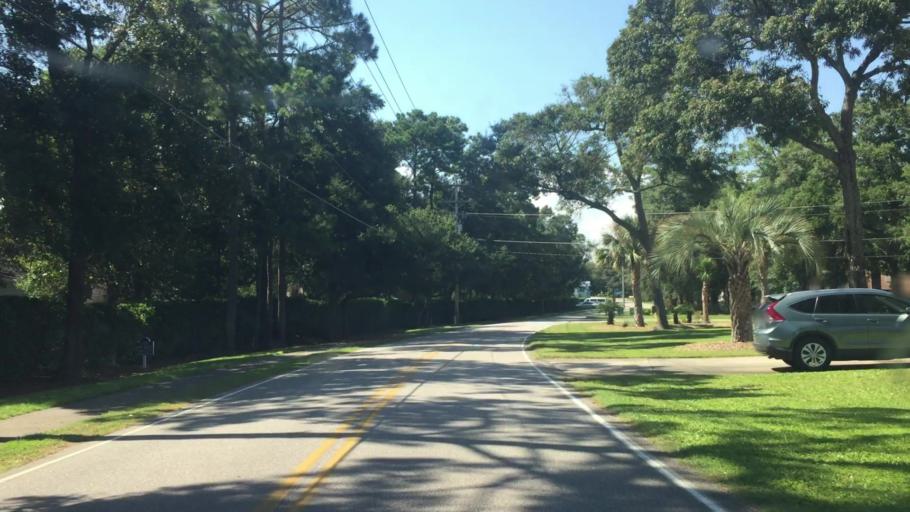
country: US
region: South Carolina
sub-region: Horry County
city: North Myrtle Beach
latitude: 33.8257
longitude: -78.6651
